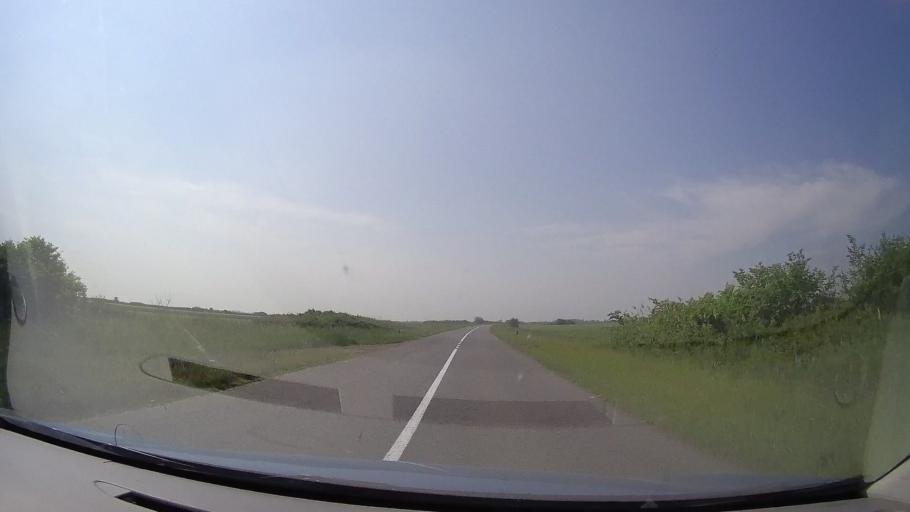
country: RS
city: Jarkovac
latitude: 45.2960
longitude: 20.7638
